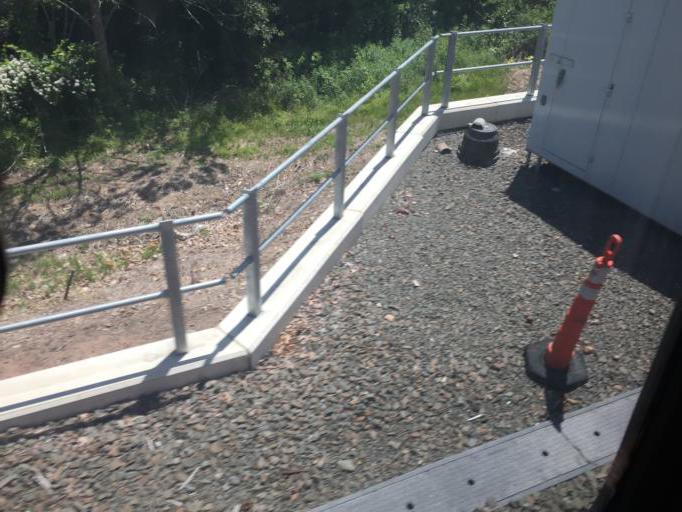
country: US
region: Connecticut
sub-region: New Haven County
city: Meriden
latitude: 41.5108
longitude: -72.8144
